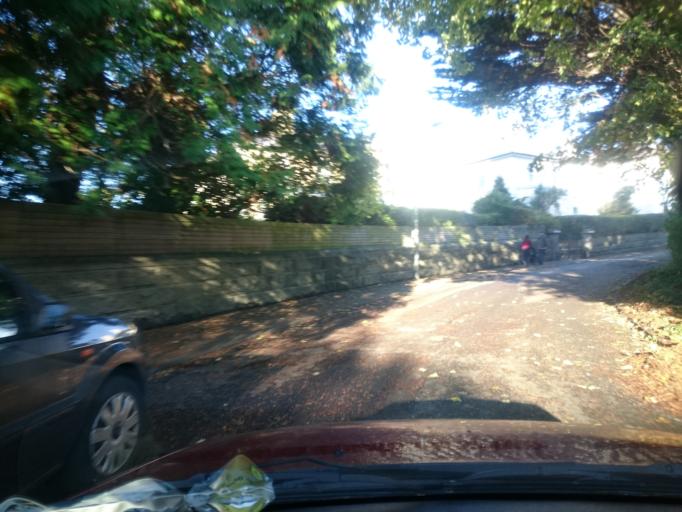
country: IE
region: Leinster
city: Monkstown
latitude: 53.2933
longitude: -6.1636
